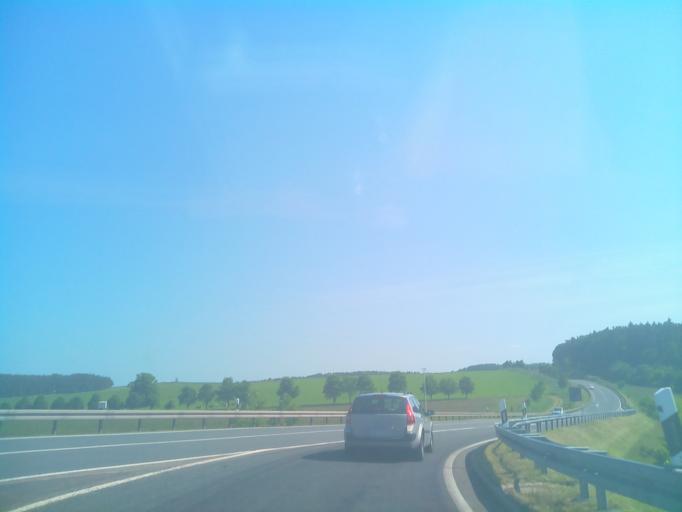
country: DE
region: Thuringia
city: Langewiesen
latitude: 50.7136
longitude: 10.9637
